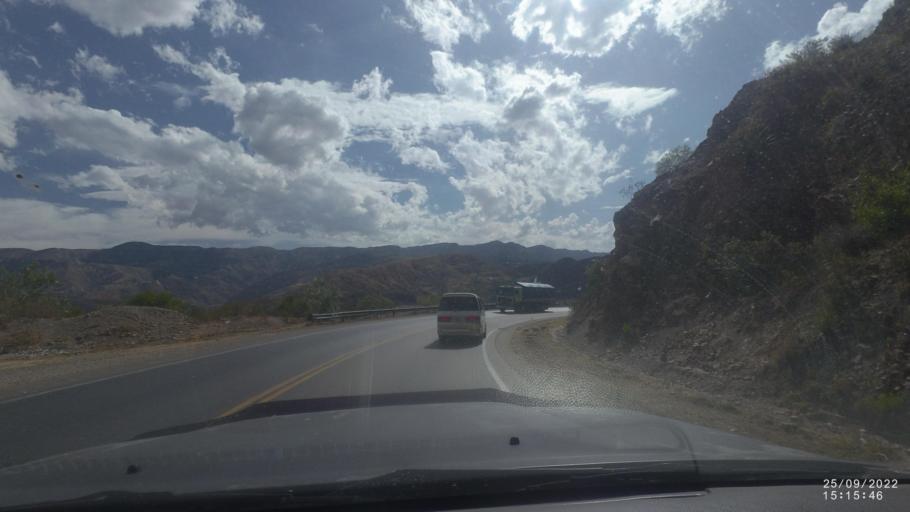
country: BO
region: Cochabamba
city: Irpa Irpa
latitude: -17.6317
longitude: -66.3921
